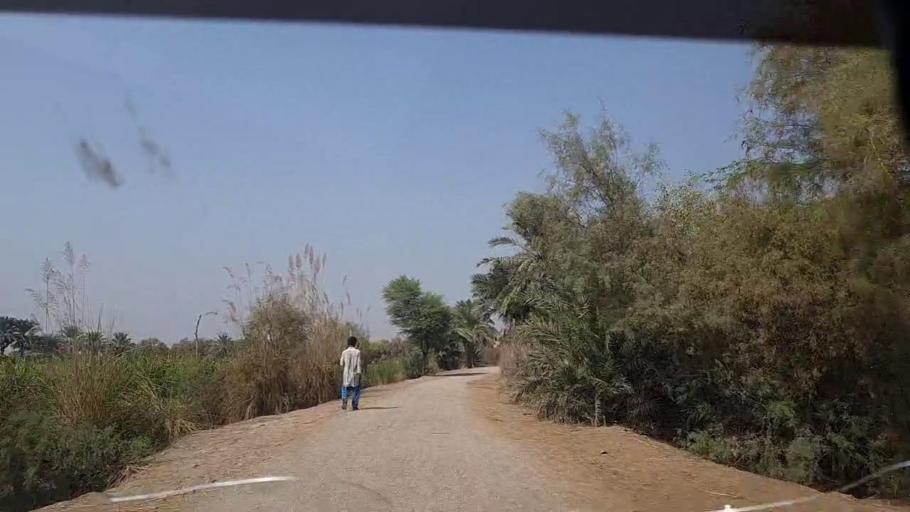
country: PK
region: Sindh
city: Shikarpur
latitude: 28.0896
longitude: 68.6692
